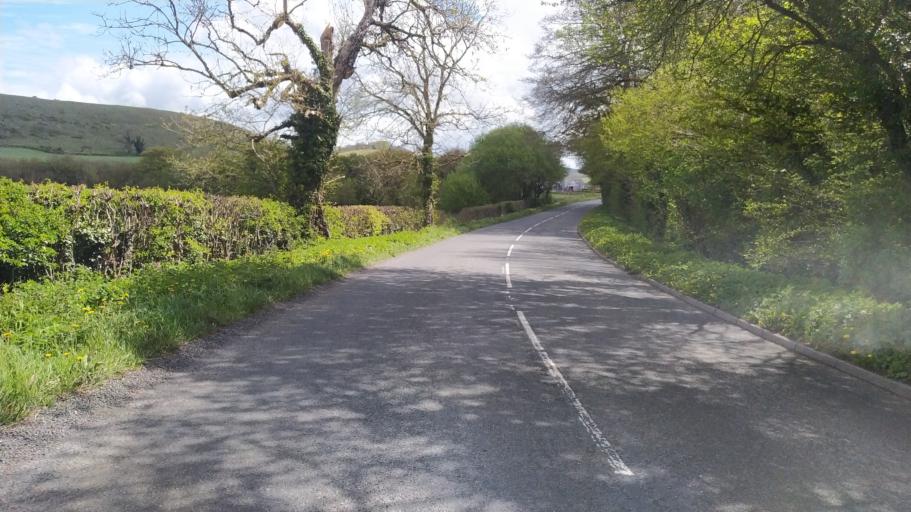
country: GB
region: England
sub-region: Wiltshire
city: Kilmington
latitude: 51.1327
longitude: -2.2991
